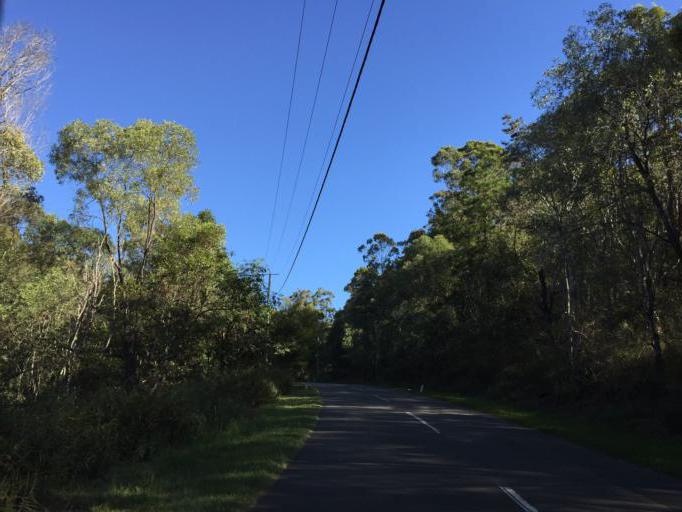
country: AU
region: Queensland
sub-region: Brisbane
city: Kenmore Hills
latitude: -27.4609
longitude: 152.9288
